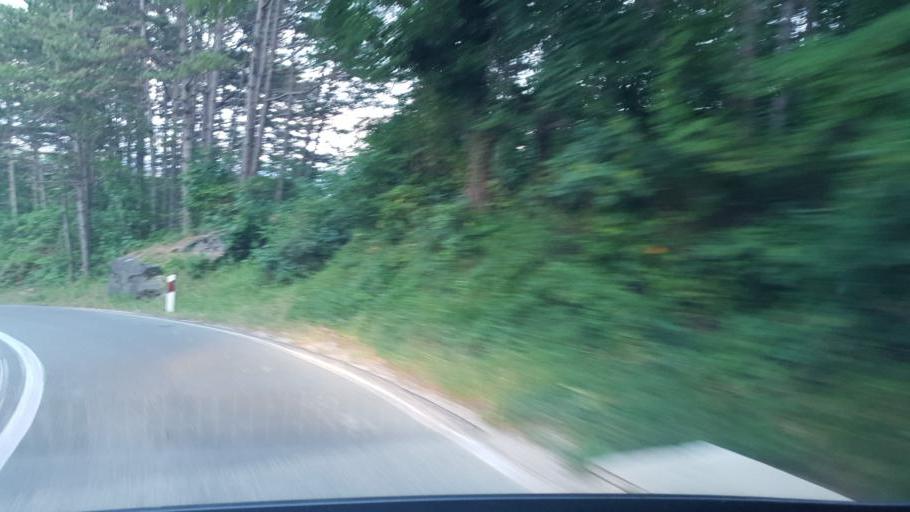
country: HR
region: Primorsko-Goranska
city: Punat
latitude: 45.0269
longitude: 14.6776
